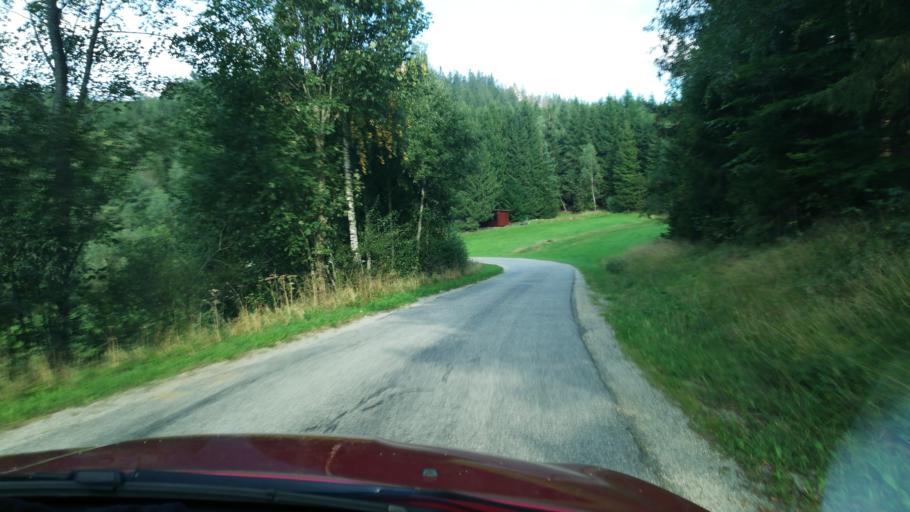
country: AT
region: Lower Austria
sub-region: Politischer Bezirk Zwettl
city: Langschlag
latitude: 48.4739
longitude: 14.8193
